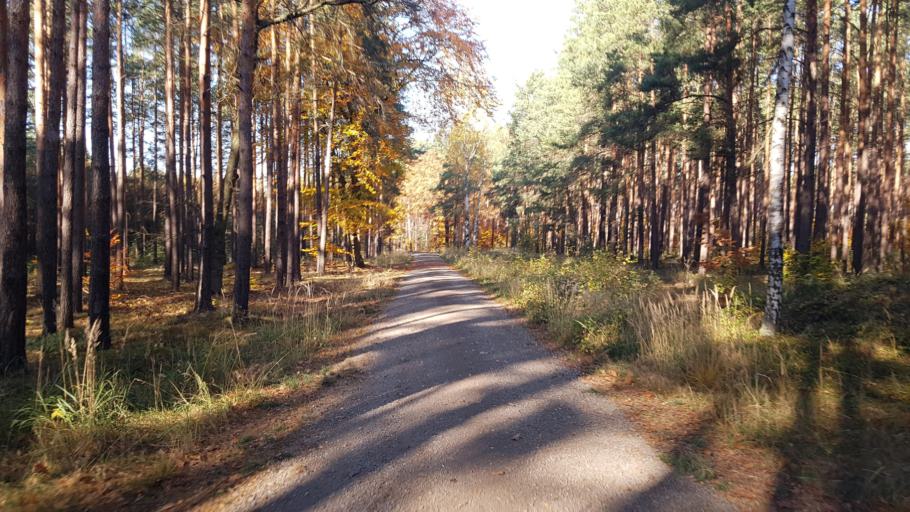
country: DE
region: Brandenburg
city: Ruckersdorf
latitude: 51.5607
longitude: 13.6235
